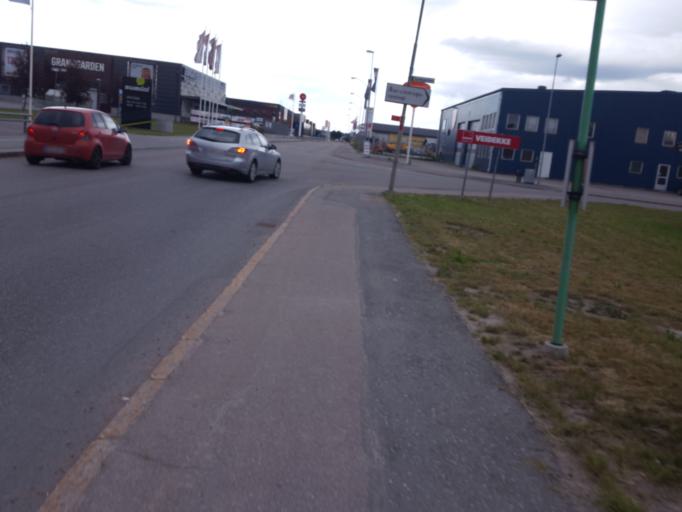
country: SE
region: Uppsala
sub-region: Uppsala Kommun
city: Saevja
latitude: 59.8471
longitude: 17.6804
